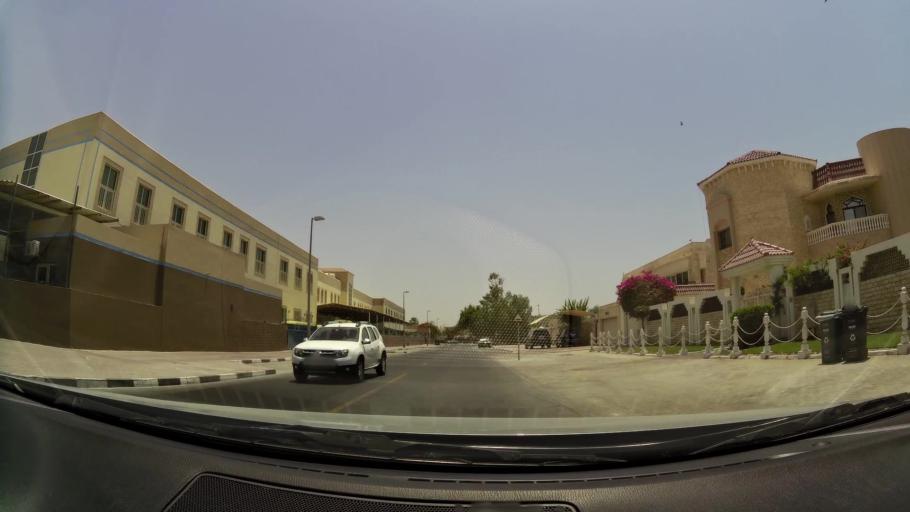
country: AE
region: Dubai
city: Dubai
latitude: 25.2139
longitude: 55.2553
